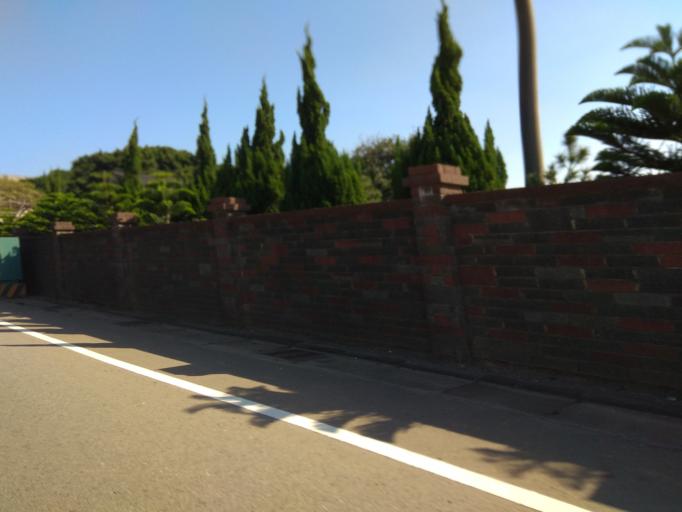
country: TW
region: Taiwan
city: Taoyuan City
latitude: 25.0355
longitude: 121.1108
